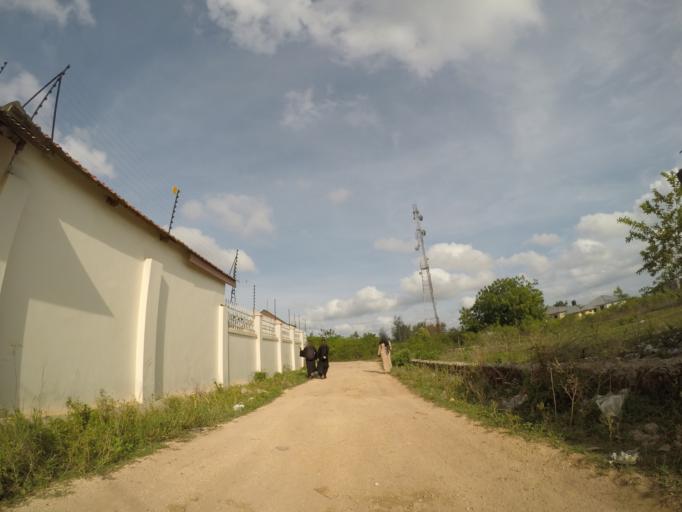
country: TZ
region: Zanzibar Central/South
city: Koani
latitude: -6.2274
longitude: 39.3153
